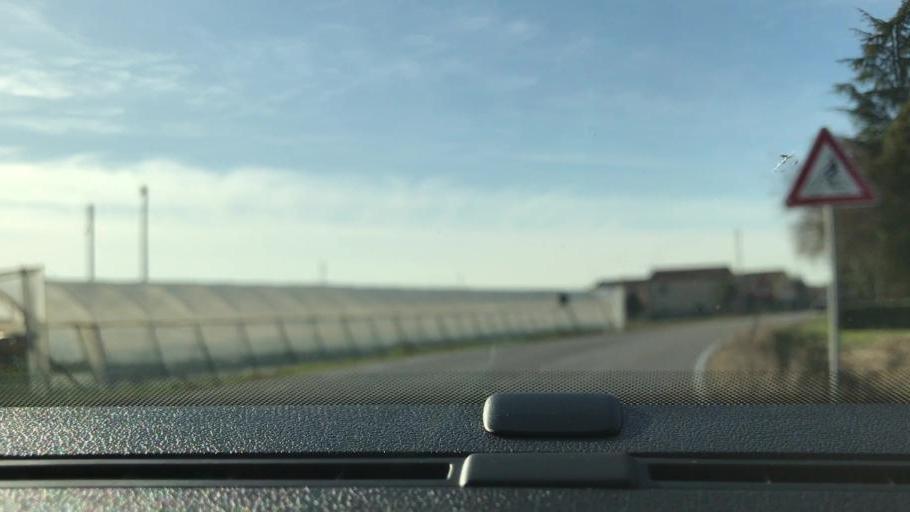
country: IT
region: Veneto
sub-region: Provincia di Rovigo
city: Baruchella
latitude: 45.0693
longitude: 11.4585
